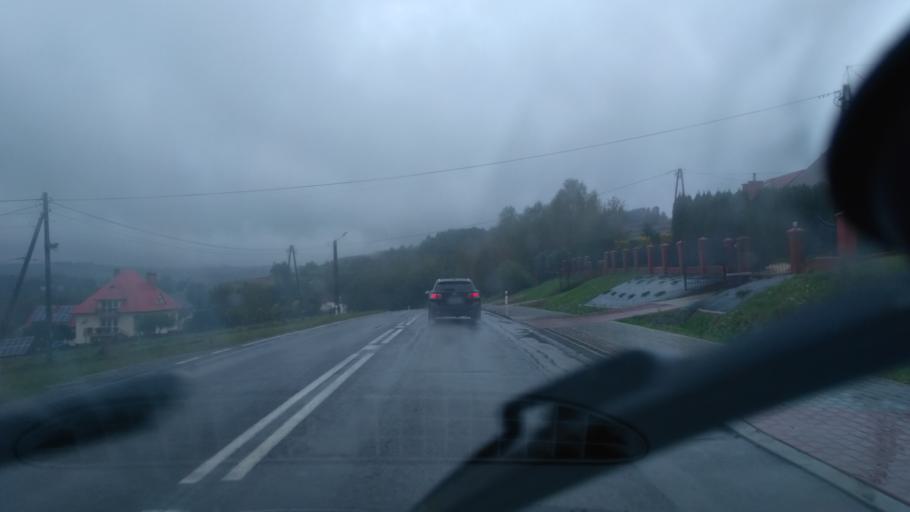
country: PL
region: Subcarpathian Voivodeship
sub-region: Powiat ropczycko-sedziszowski
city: Niedzwiada
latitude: 50.0013
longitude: 21.5606
